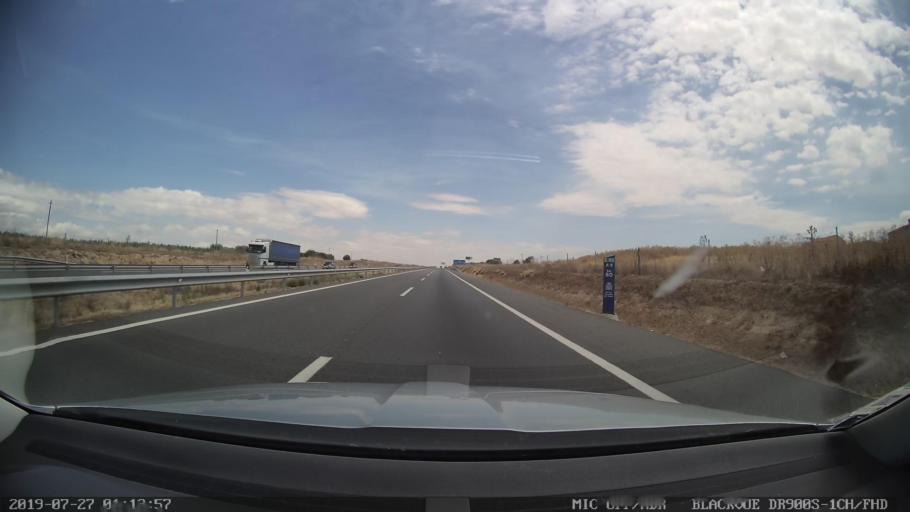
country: ES
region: Castille-La Mancha
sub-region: Province of Toledo
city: Santa Olalla
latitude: 40.0337
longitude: -4.4273
